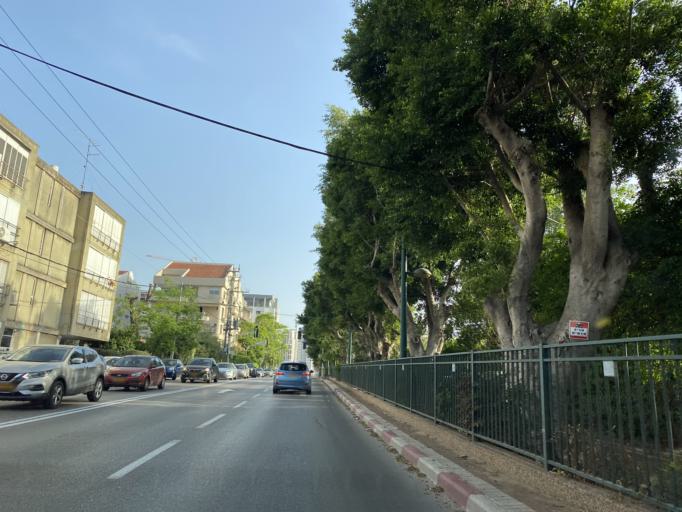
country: IL
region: Central District
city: Kfar Saba
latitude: 32.1731
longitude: 34.9016
